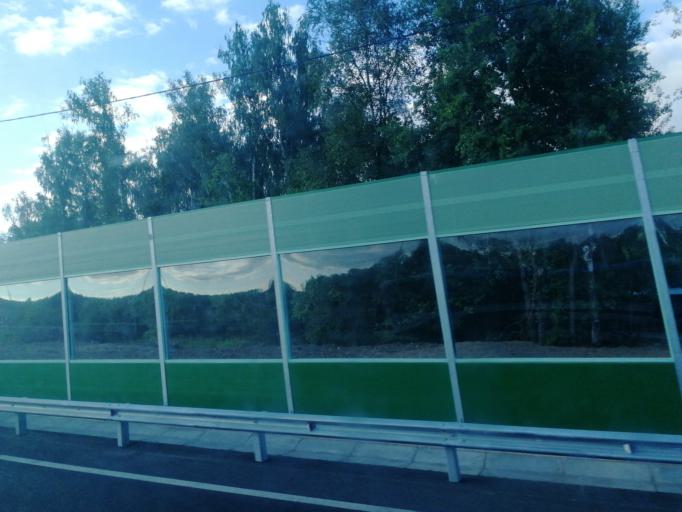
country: RU
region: Kaluga
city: Kaluga
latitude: 54.4582
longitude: 36.2773
